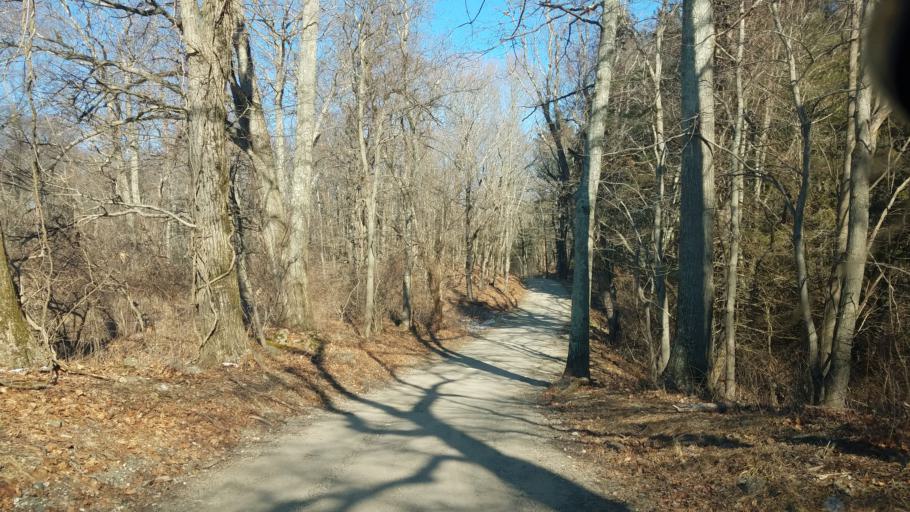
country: US
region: Connecticut
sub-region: New Haven County
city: Heritage Village
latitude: 41.5086
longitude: -73.2831
